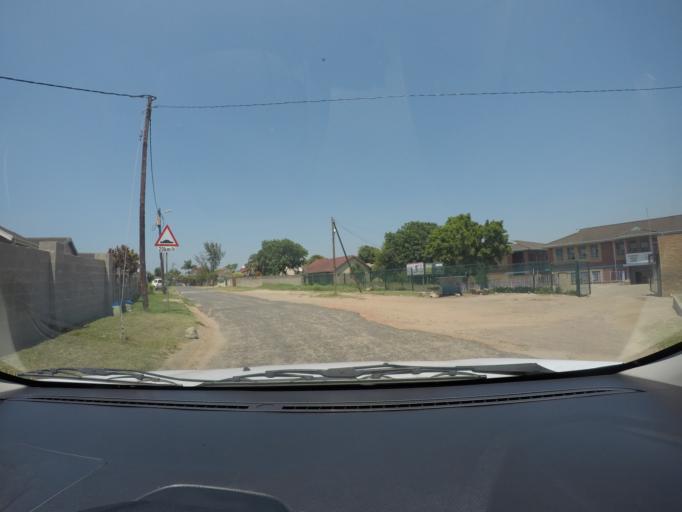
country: ZA
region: KwaZulu-Natal
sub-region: uThungulu District Municipality
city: eSikhawini
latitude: -28.8684
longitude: 31.9221
